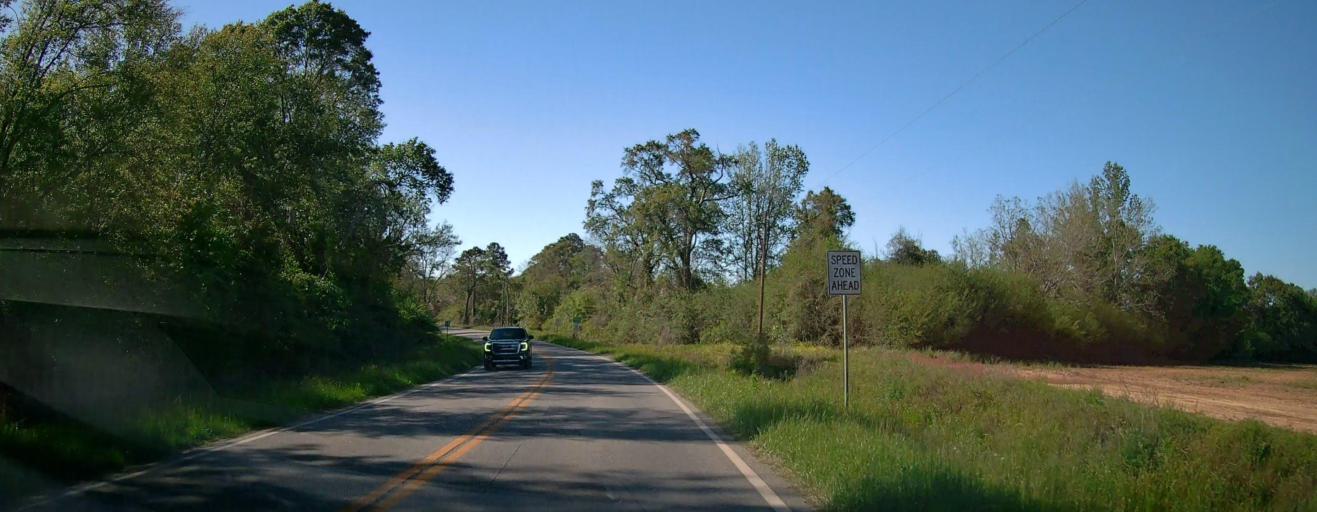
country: US
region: Georgia
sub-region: Wilcox County
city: Rochelle
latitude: 31.9448
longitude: -83.4441
